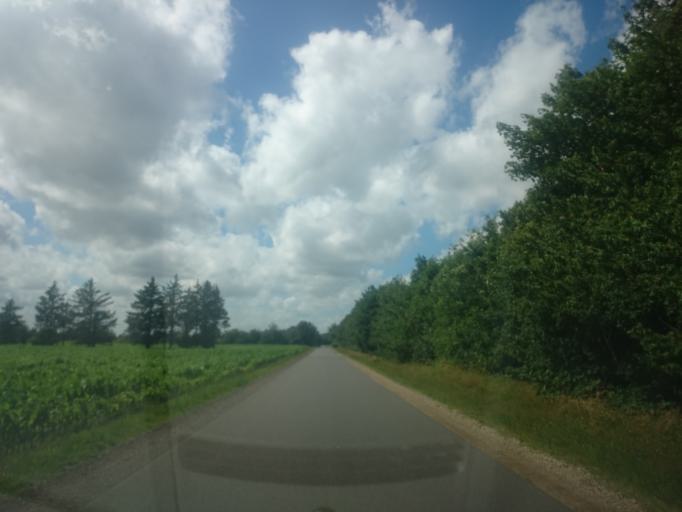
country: DK
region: South Denmark
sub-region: Billund Kommune
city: Billund
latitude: 55.7338
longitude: 9.1962
